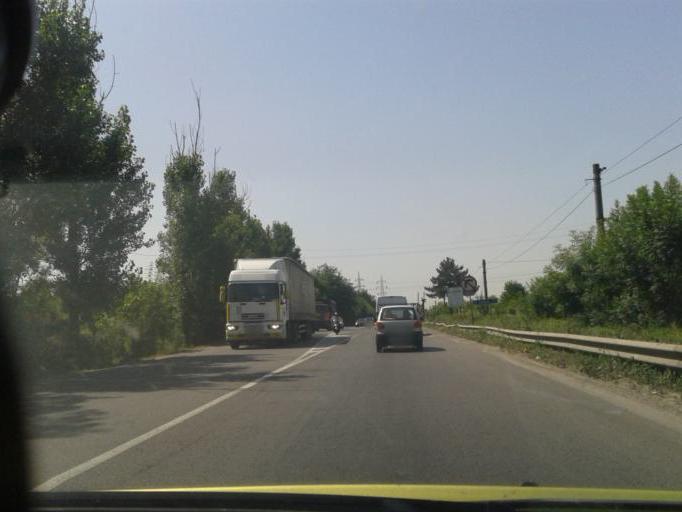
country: RO
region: Ilfov
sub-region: Comuna Pantelimon
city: Pantelimon
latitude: 44.4448
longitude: 26.2357
